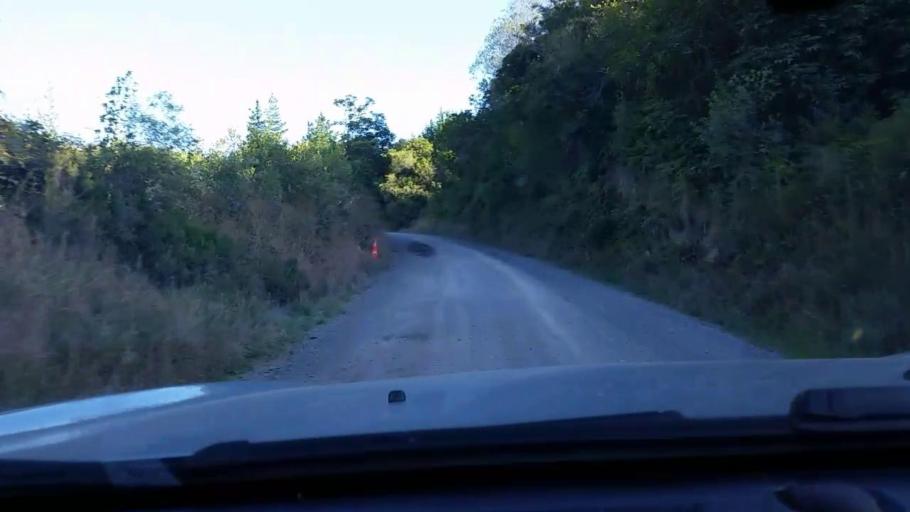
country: NZ
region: Waikato
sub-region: Taupo District
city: Taupo
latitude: -38.4589
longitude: 176.1590
